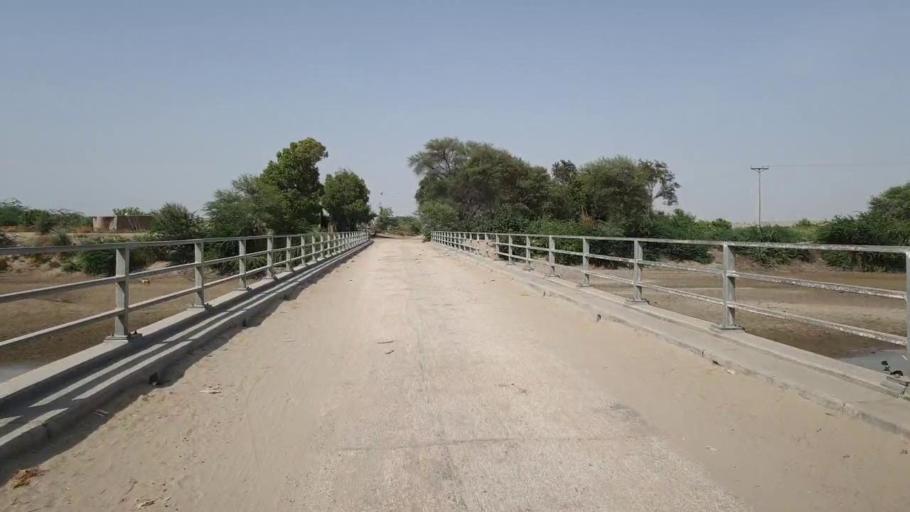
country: PK
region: Sindh
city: Jam Sahib
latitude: 26.4098
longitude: 68.9068
